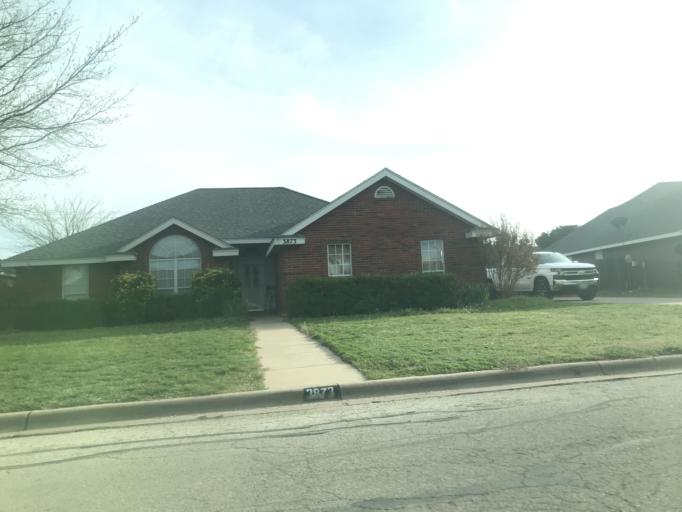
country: US
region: Texas
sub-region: Taylor County
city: Abilene
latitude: 32.3953
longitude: -99.7731
